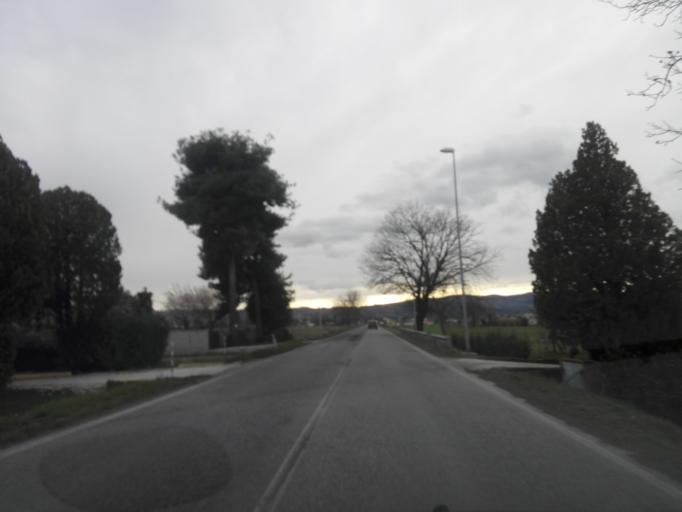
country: IT
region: Umbria
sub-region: Provincia di Perugia
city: Spello
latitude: 42.9514
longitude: 12.6565
